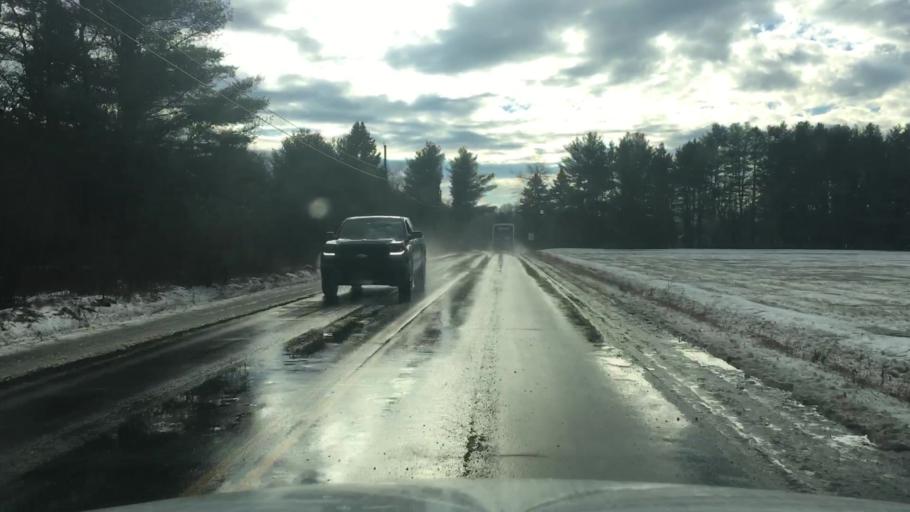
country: US
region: Maine
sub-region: Penobscot County
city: Brewer
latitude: 44.7442
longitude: -68.7659
